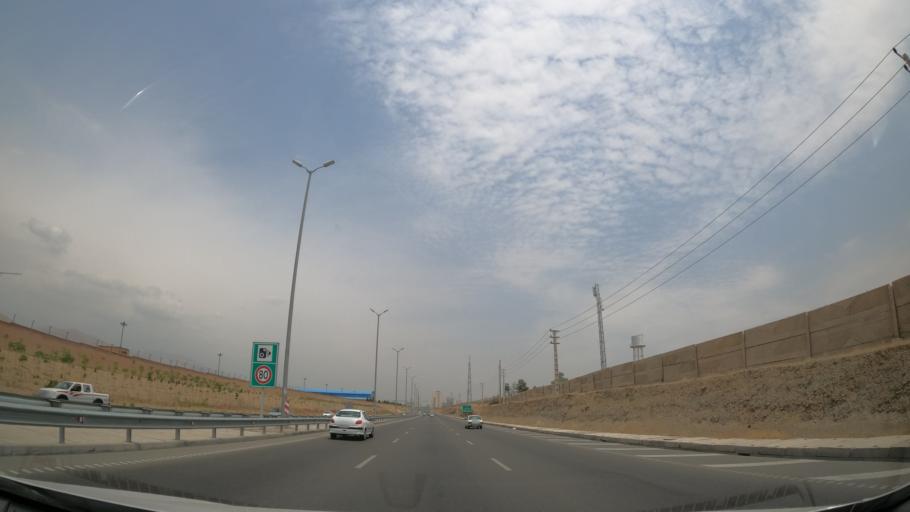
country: IR
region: Tehran
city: Shahr-e Qods
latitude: 35.7393
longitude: 51.2258
